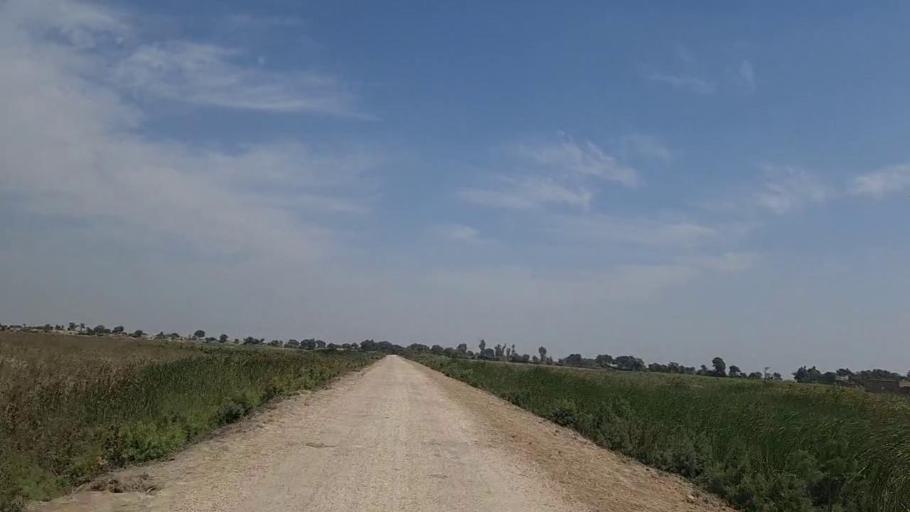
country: PK
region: Sindh
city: Mirpur Batoro
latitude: 24.6684
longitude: 68.2855
